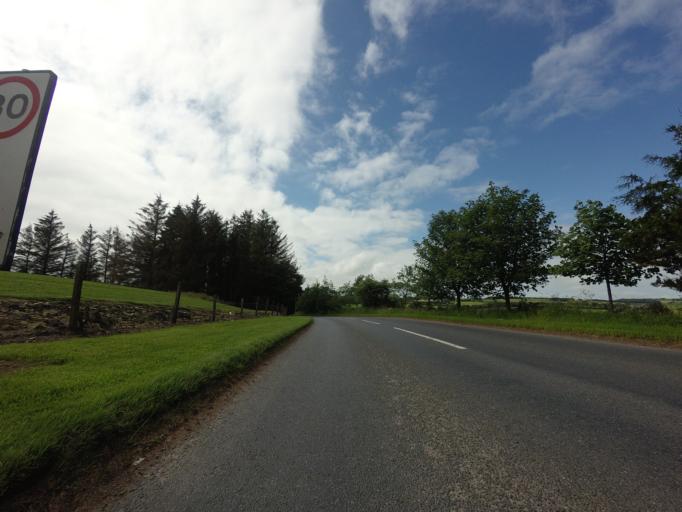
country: GB
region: Scotland
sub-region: Aberdeenshire
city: Turriff
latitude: 57.5439
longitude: -2.3183
